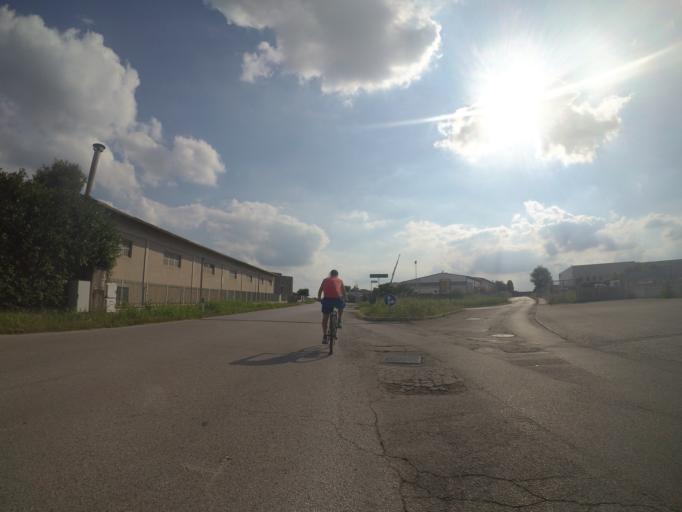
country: IT
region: Friuli Venezia Giulia
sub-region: Provincia di Udine
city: Fagagna
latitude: 46.0998
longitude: 13.0944
